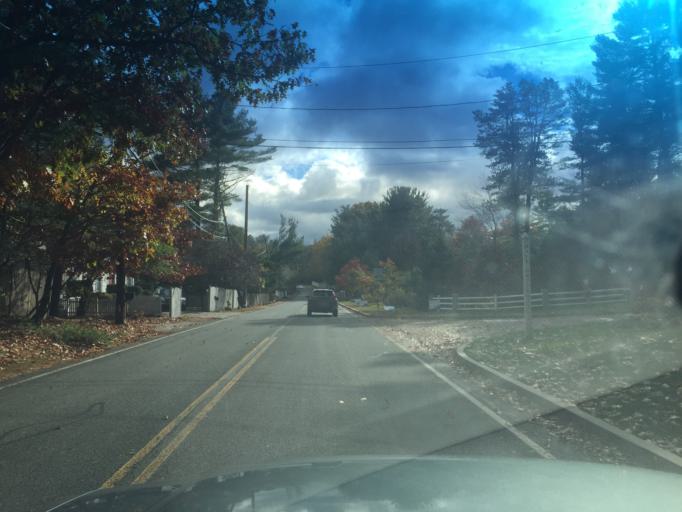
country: US
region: Massachusetts
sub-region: Norfolk County
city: Needham
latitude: 42.2669
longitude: -71.2164
